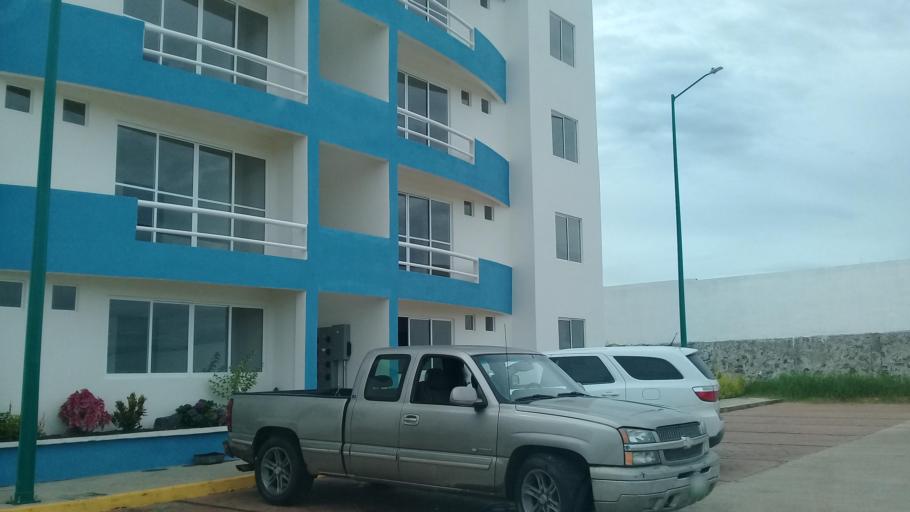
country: MX
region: Veracruz
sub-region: Emiliano Zapata
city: Dos Rios
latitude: 19.4804
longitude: -96.8006
